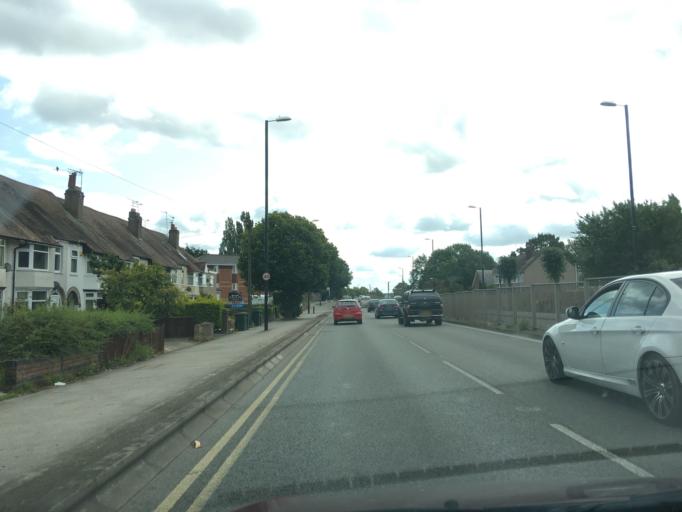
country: GB
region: England
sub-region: Coventry
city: Coventry
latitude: 52.3847
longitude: -1.5300
